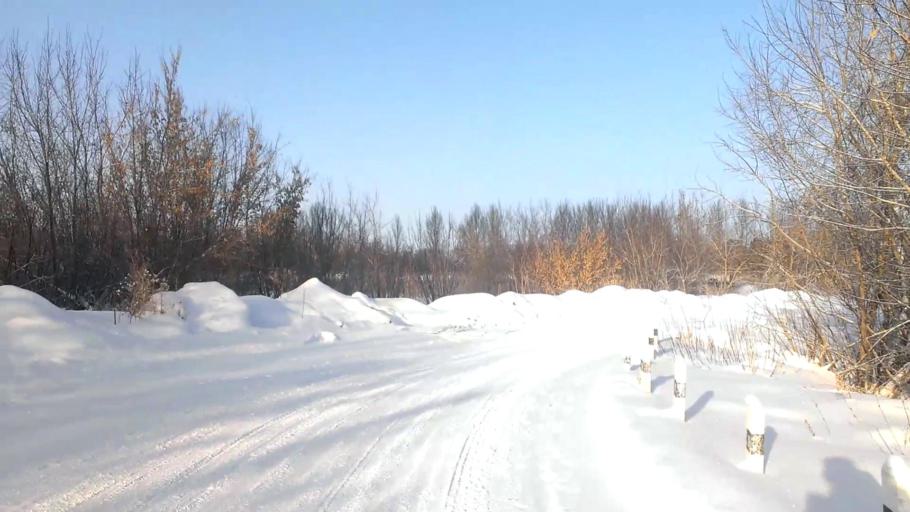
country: RU
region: Altai Krai
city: Novosilikatnyy
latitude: 53.3462
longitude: 83.6292
